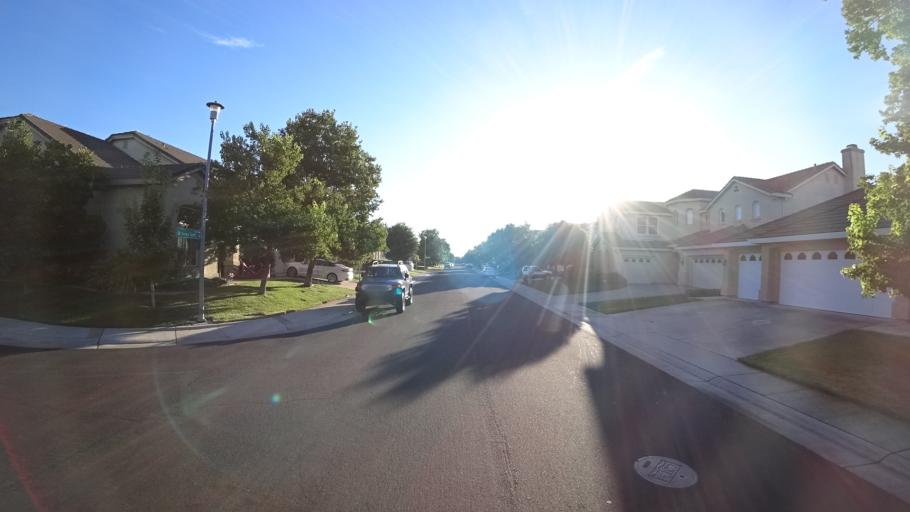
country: US
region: California
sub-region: Sacramento County
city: Laguna
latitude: 38.3951
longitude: -121.4788
